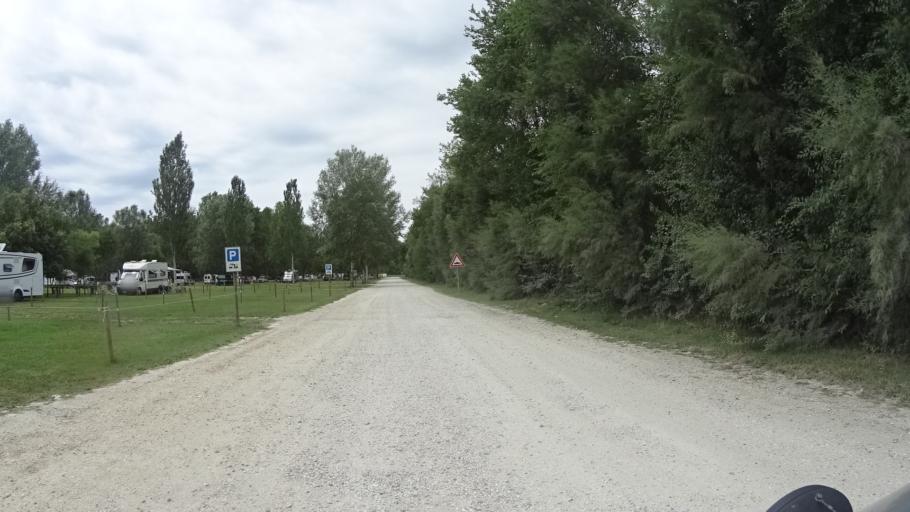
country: IT
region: Veneto
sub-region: Provincia di Venezia
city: Bibione
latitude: 45.6242
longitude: 12.9555
